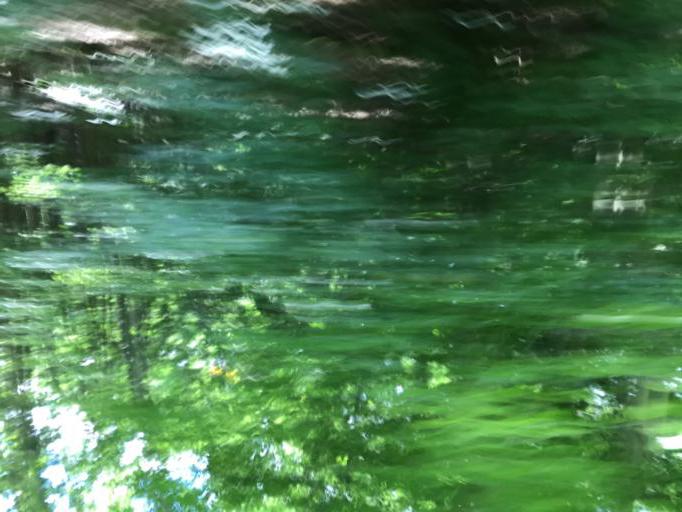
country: DE
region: Saxony-Anhalt
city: Stapelburg
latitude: 51.8997
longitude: 10.6385
